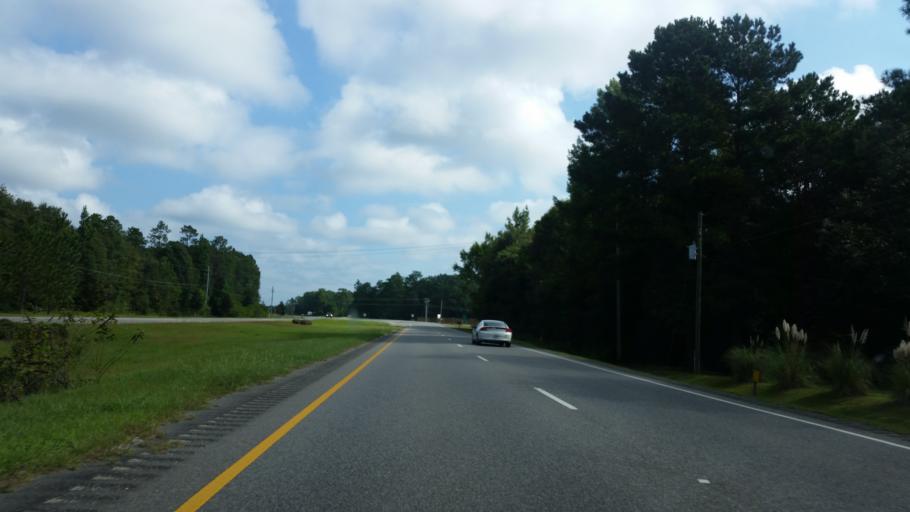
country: US
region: Alabama
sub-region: Baldwin County
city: Bay Minette
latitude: 30.9152
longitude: -87.7787
